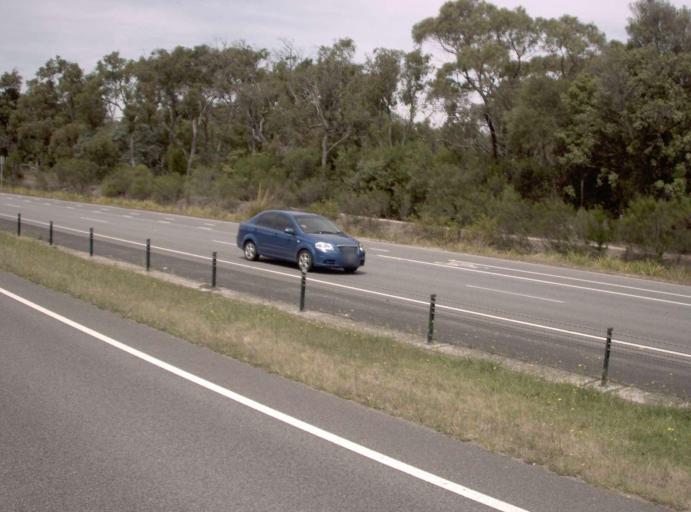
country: AU
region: Victoria
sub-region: Casey
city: Cranbourne South
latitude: -38.1462
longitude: 145.2260
